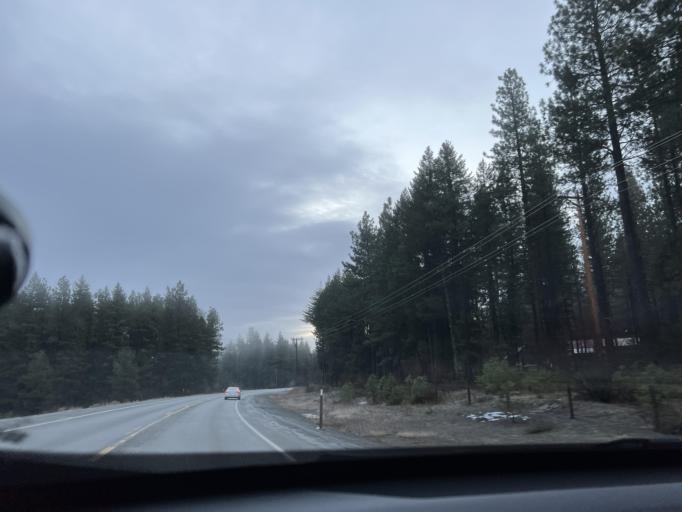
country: US
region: Washington
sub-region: Chelan County
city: Granite Falls
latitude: 48.5685
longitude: -120.3751
